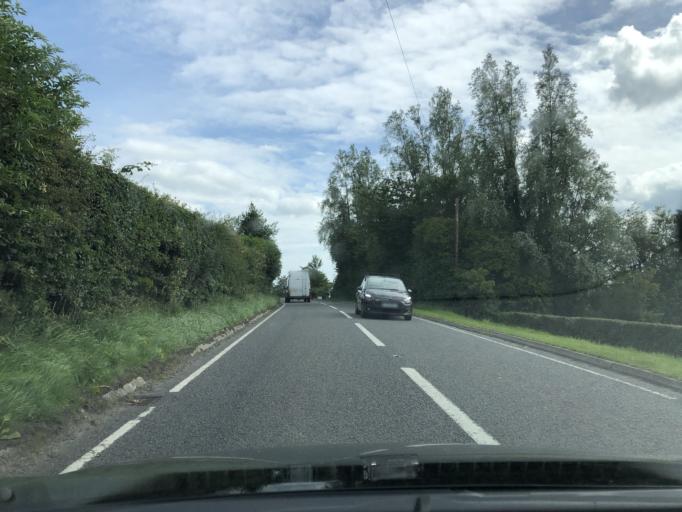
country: GB
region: Northern Ireland
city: Ballynahinch
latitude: 54.4272
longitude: -5.9248
